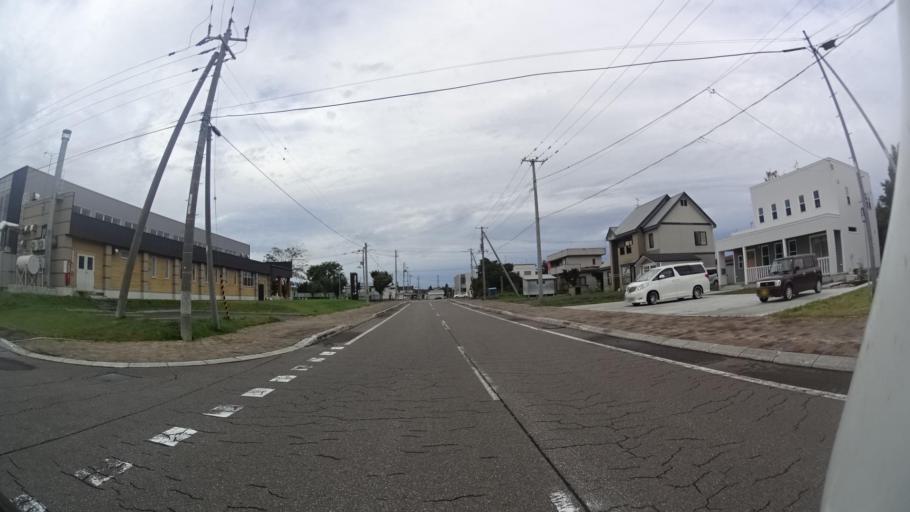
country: JP
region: Hokkaido
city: Abashiri
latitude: 43.8350
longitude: 144.5988
